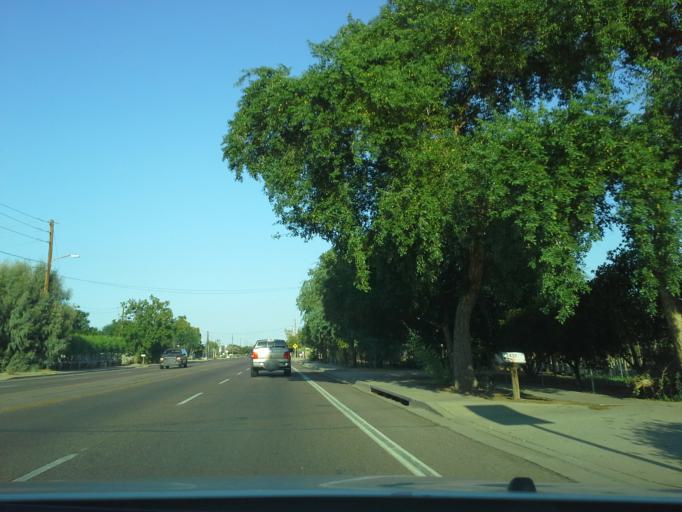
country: US
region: Arizona
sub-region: Maricopa County
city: Guadalupe
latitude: 33.3926
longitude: -112.0073
